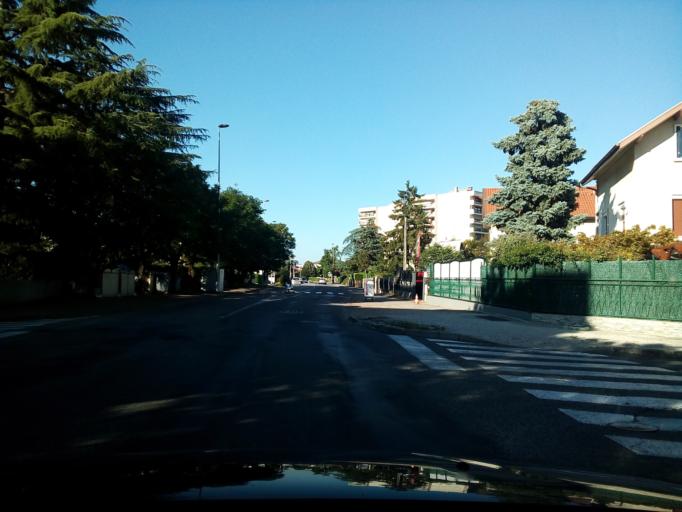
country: FR
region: Rhone-Alpes
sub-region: Departement de l'Isere
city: Echirolles
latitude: 45.1443
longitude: 5.7242
